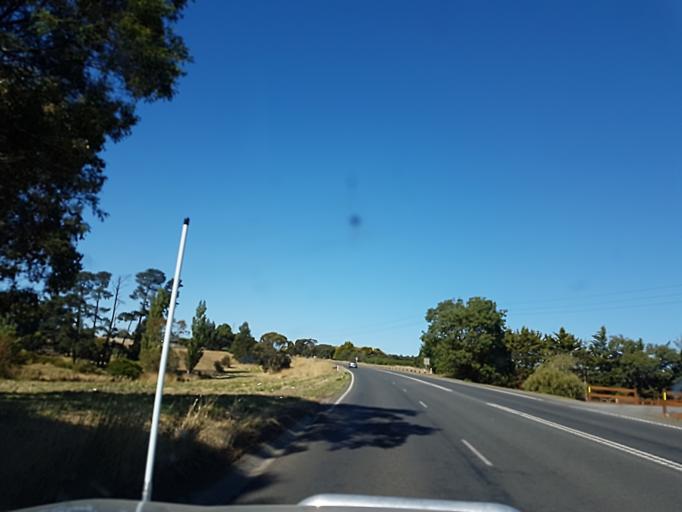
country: AU
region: Victoria
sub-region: Colac-Otway
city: Colac
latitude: -38.3340
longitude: 143.6151
